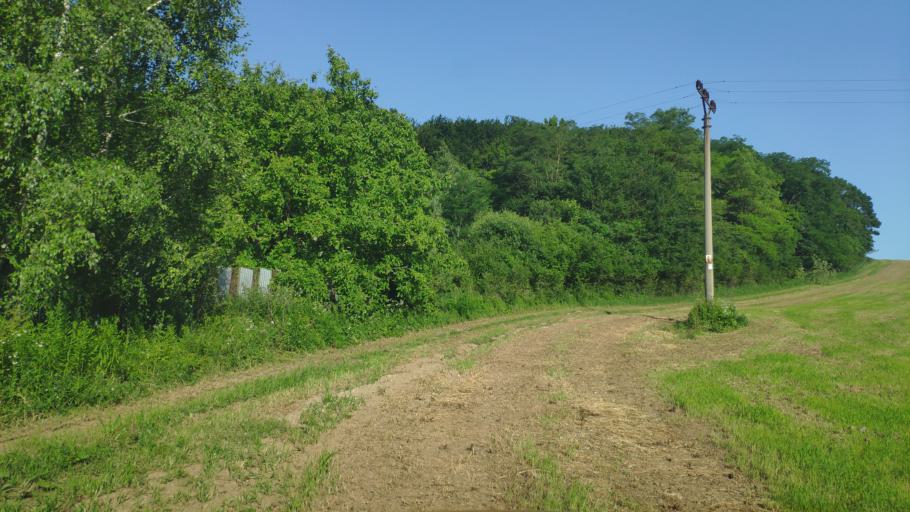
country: SK
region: Kosicky
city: Kosice
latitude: 48.8306
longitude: 21.2238
